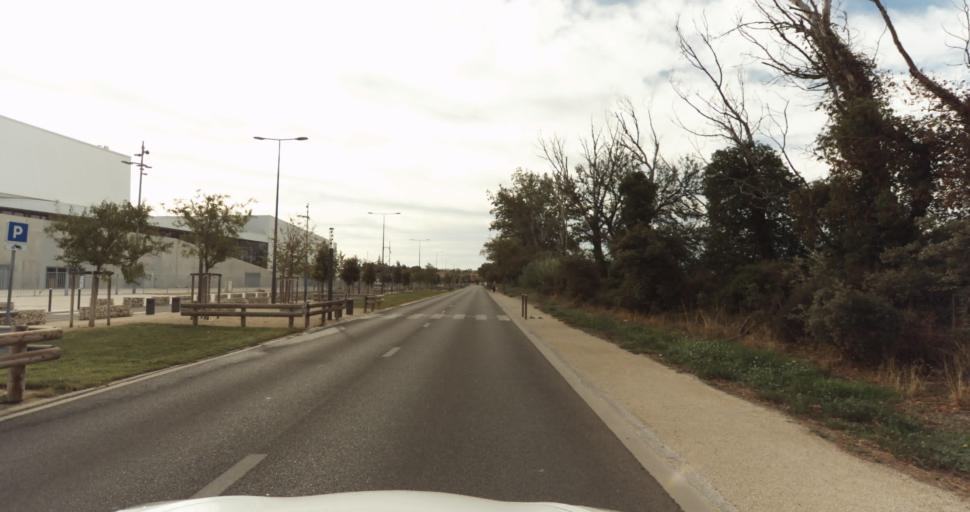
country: FR
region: Provence-Alpes-Cote d'Azur
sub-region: Departement des Bouches-du-Rhone
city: Miramas
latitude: 43.5936
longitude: 4.9982
